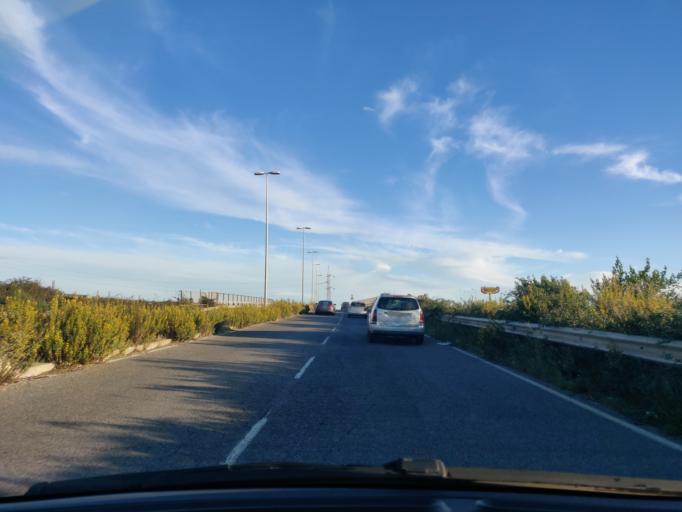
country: IT
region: Latium
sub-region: Citta metropolitana di Roma Capitale
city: Civitavecchia
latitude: 42.1093
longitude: 11.7856
